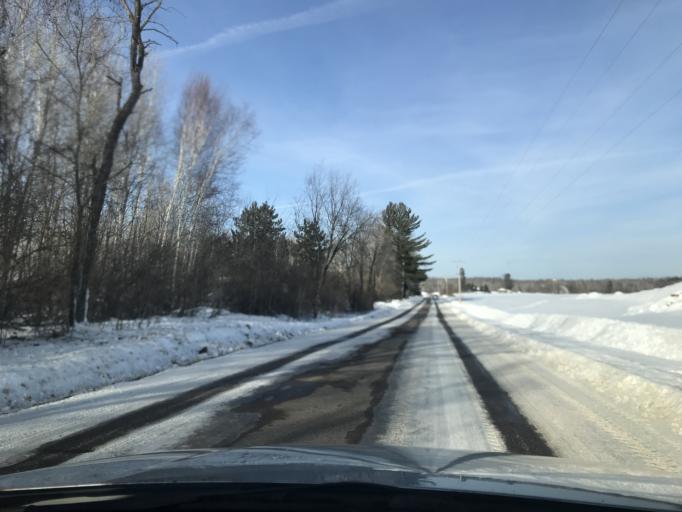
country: US
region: Wisconsin
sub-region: Menominee County
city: Legend Lake
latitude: 45.3098
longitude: -88.5219
